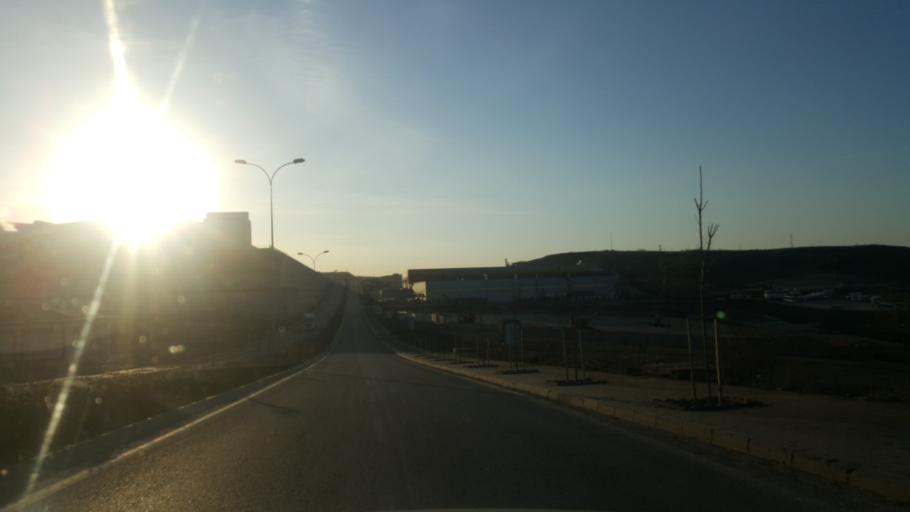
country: TR
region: Kocaeli
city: Tavsanli
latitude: 40.8344
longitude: 29.5501
